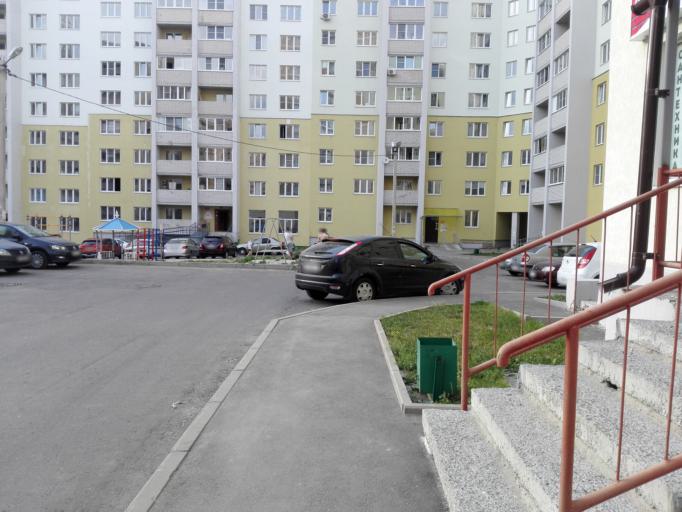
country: RU
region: Vladimir
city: Raduzhnyy
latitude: 56.1085
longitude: 40.2772
